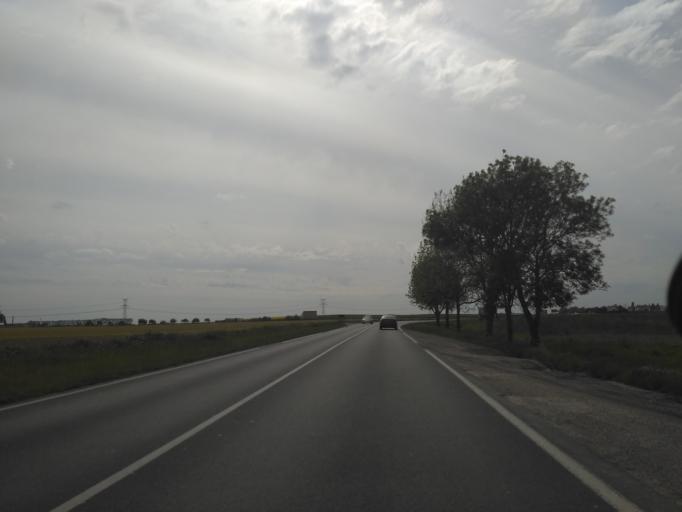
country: FR
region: Ile-de-France
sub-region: Departement de Seine-et-Marne
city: Guignes
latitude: 48.6360
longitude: 2.7856
